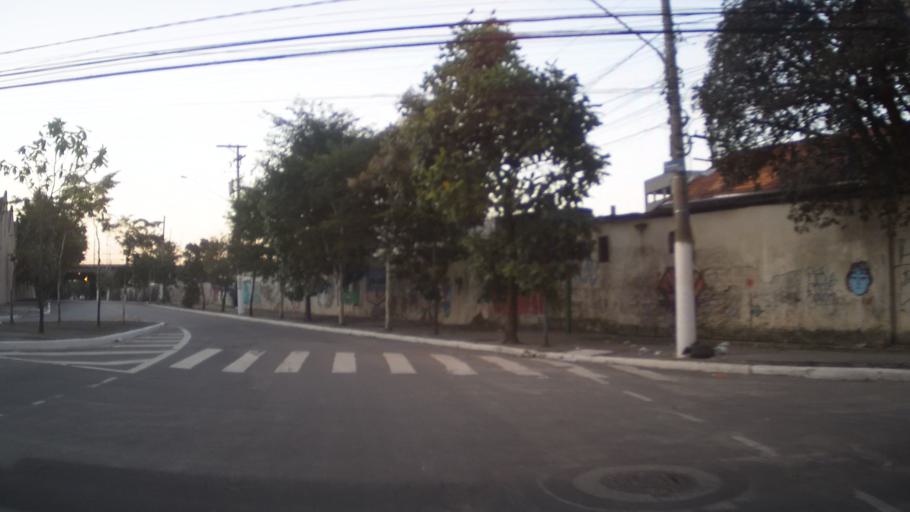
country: BR
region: Sao Paulo
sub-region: Sao Paulo
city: Sao Paulo
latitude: -23.5548
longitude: -46.6107
